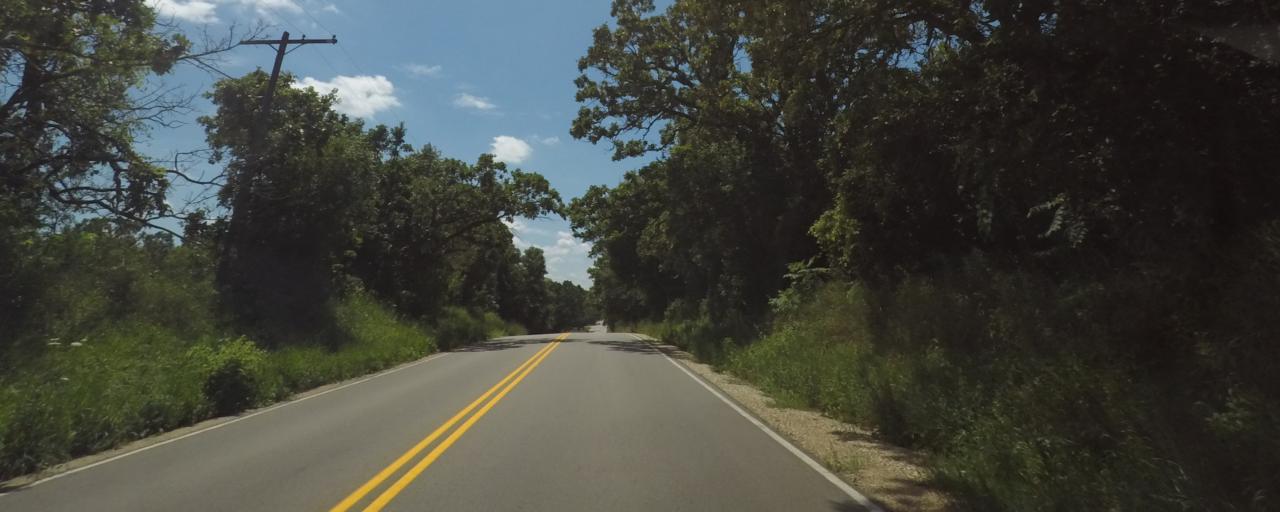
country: US
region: Wisconsin
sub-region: Waukesha County
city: Dousman
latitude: 42.9605
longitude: -88.4681
